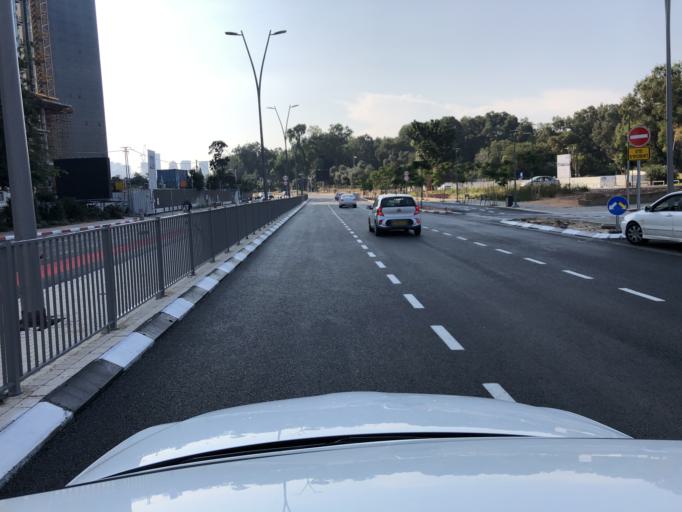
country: IL
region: Tel Aviv
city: Bene Beraq
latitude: 32.0976
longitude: 34.8236
